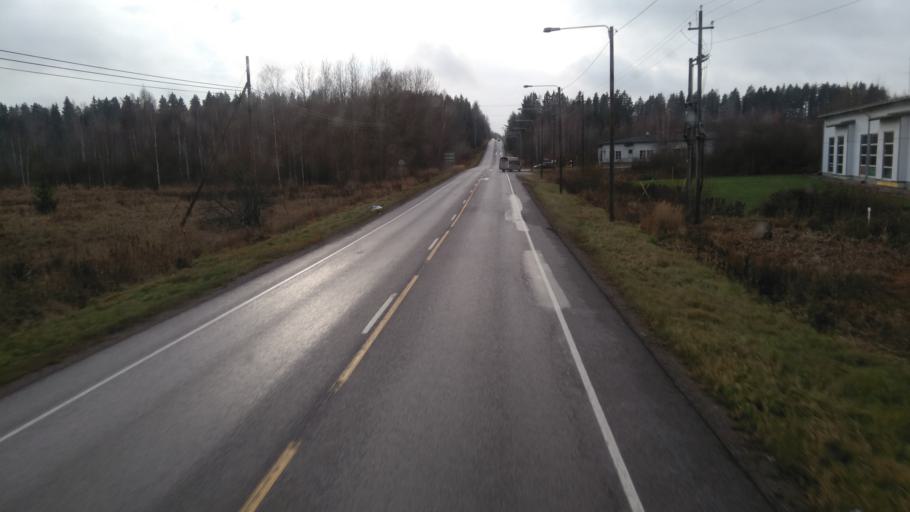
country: FI
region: Uusimaa
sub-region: Porvoo
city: Porvoo
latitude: 60.4085
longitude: 25.6949
